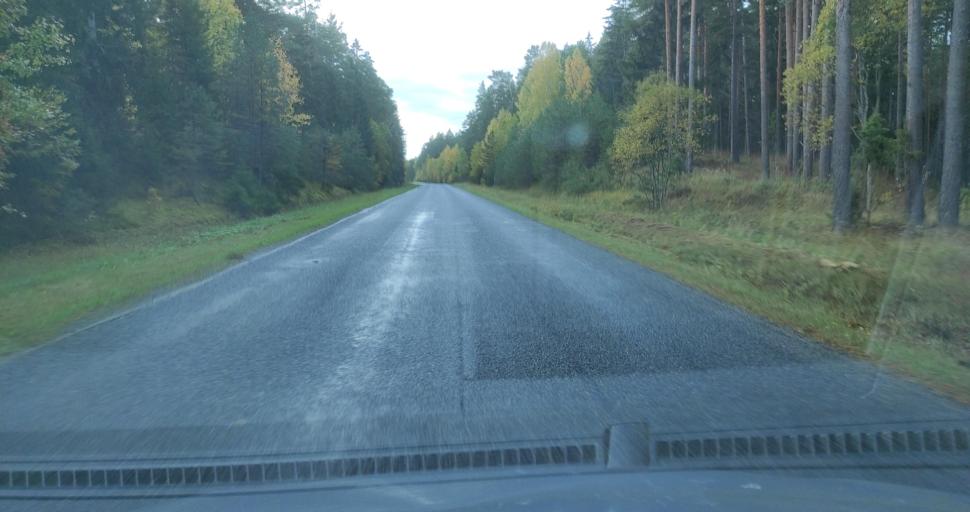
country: LV
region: Skrunda
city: Skrunda
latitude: 56.6447
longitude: 22.0103
